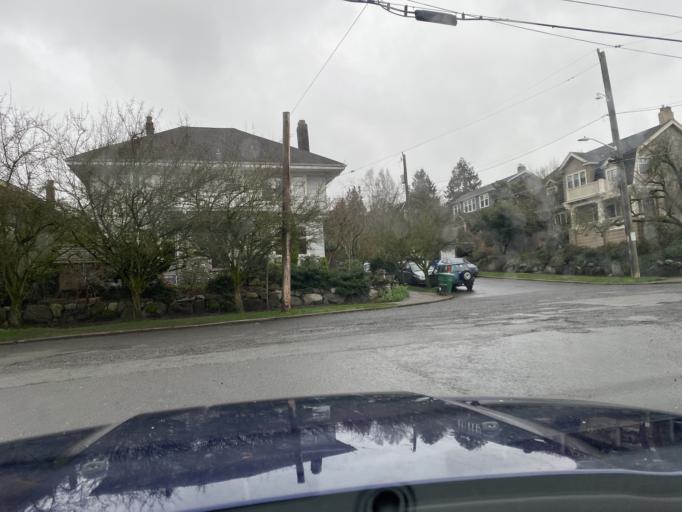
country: US
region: Washington
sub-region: King County
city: Seattle
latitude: 47.6397
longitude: -122.3170
